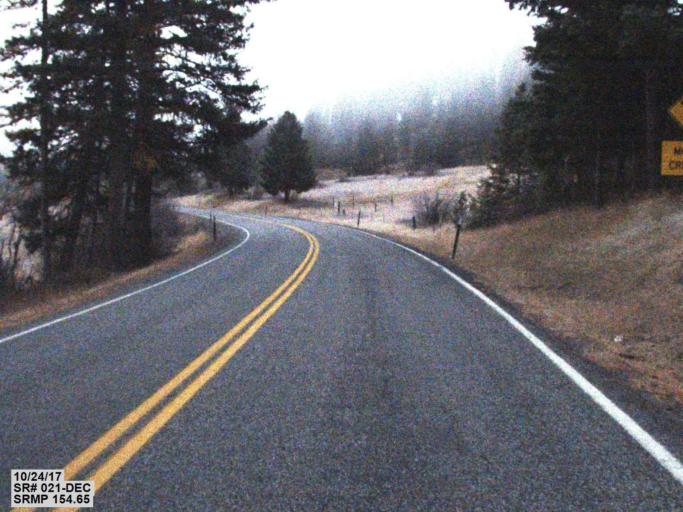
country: US
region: Washington
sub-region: Ferry County
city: Republic
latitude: 48.5653
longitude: -118.7471
